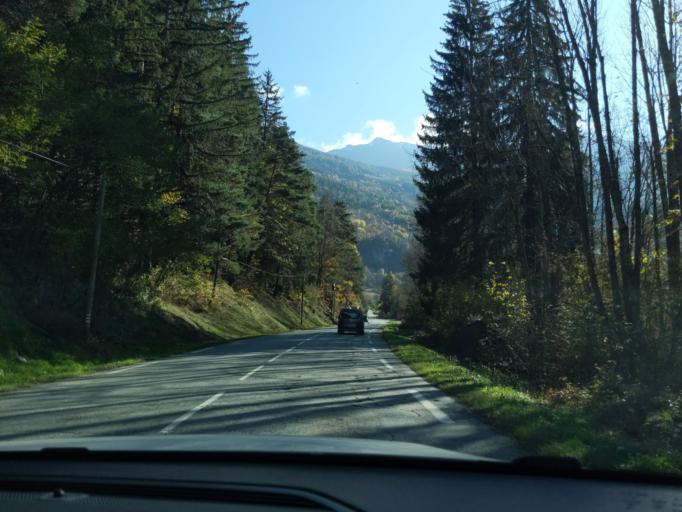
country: FR
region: Rhone-Alpes
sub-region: Departement de la Savoie
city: Seez
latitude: 45.5996
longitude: 6.8693
